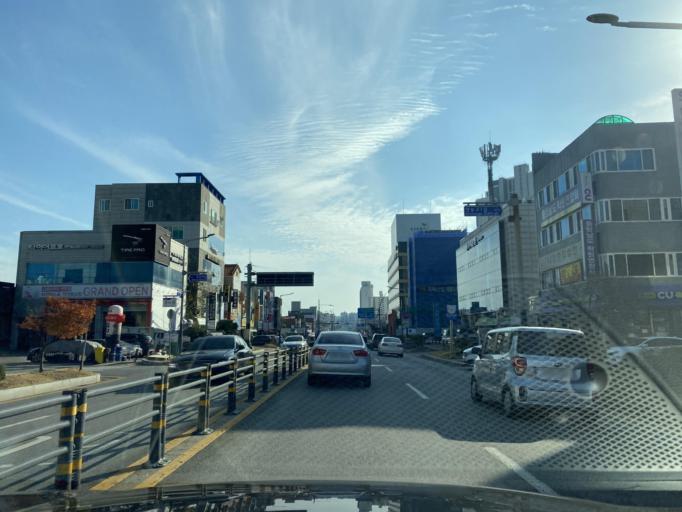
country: KR
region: Chungcheongnam-do
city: Cheonan
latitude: 36.8084
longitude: 127.1586
